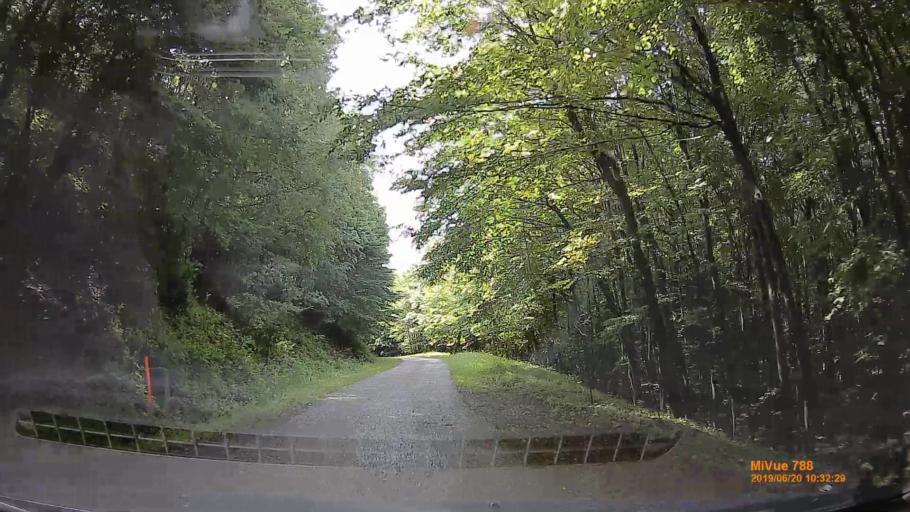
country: HU
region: Baranya
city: Mecseknadasd
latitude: 46.2069
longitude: 18.5154
